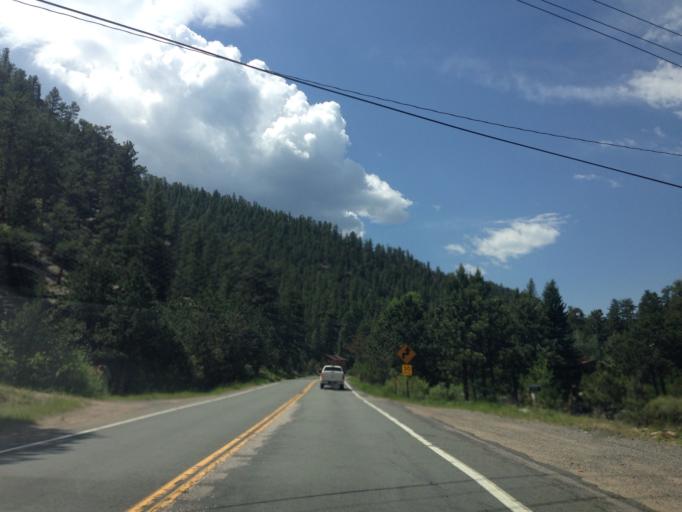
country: US
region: Colorado
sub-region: Larimer County
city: Estes Park
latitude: 40.3875
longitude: -105.4672
